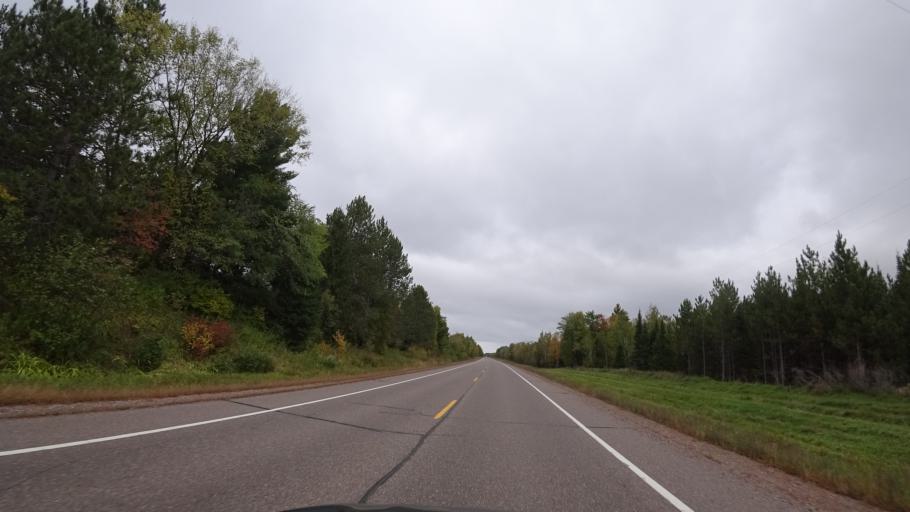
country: US
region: Wisconsin
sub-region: Rusk County
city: Ladysmith
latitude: 45.5551
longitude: -91.1118
